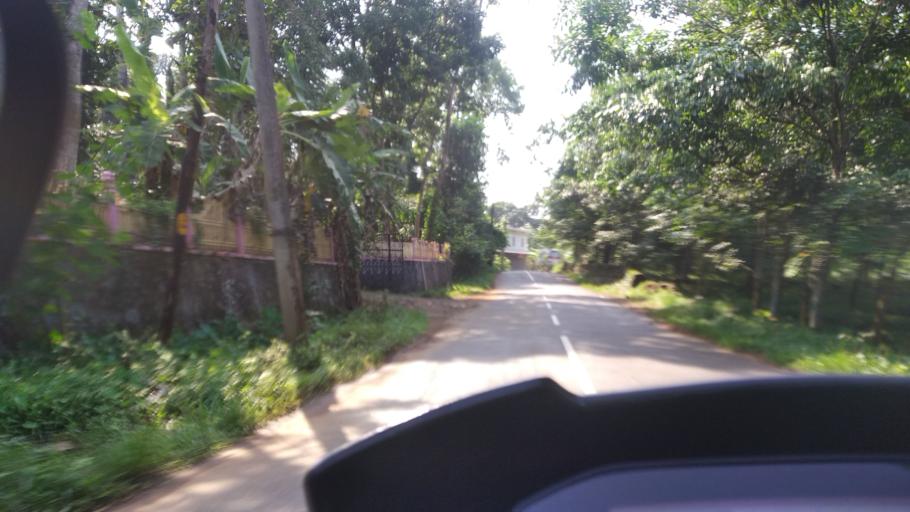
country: IN
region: Kerala
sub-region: Kottayam
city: Palackattumala
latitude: 9.8022
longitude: 76.5796
